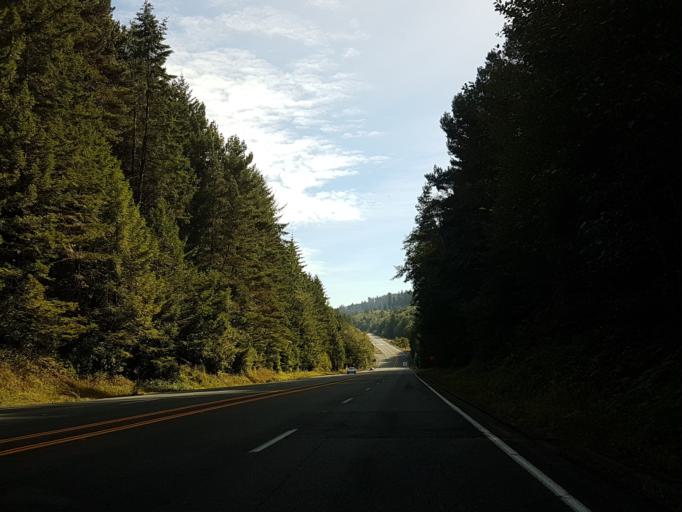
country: US
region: California
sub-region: Del Norte County
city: Bertsch-Oceanview
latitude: 41.4739
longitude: -124.0440
